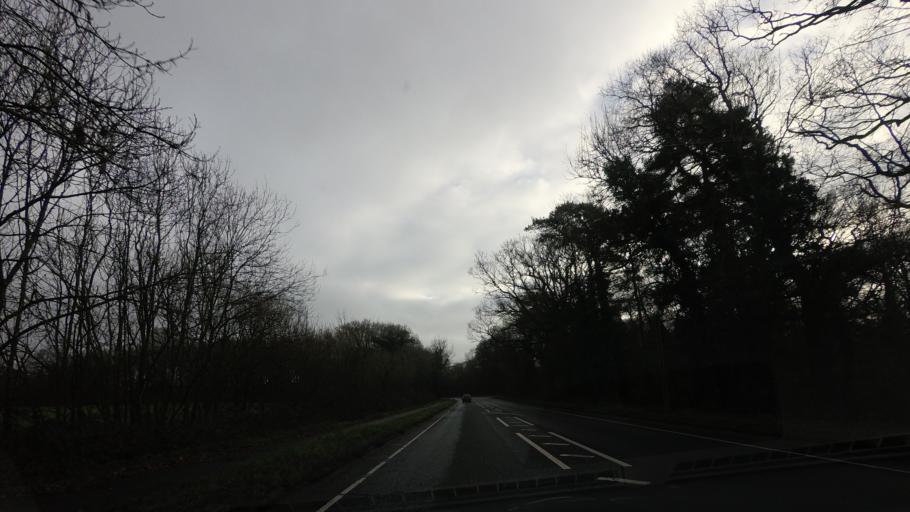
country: GB
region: England
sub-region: East Sussex
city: Robertsbridge
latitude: 51.0417
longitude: 0.4490
